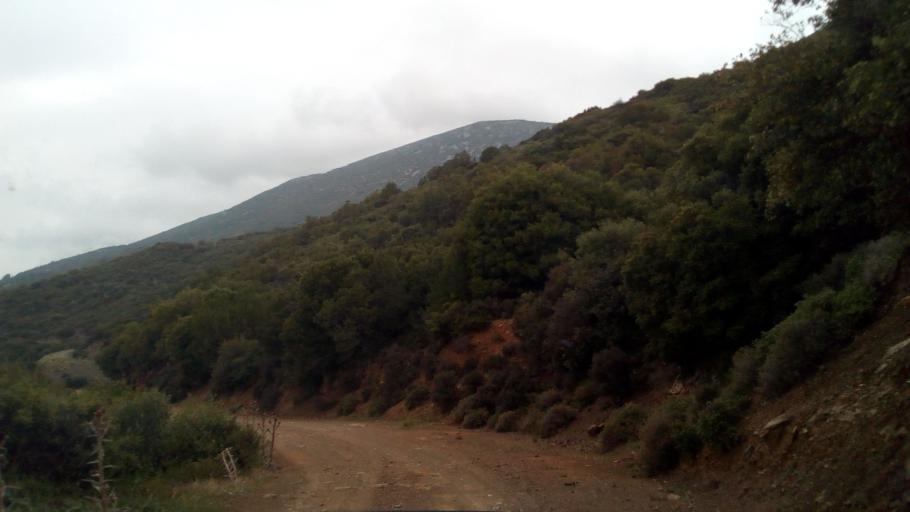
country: GR
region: West Greece
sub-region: Nomos Achaias
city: Aigio
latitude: 38.3742
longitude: 22.1563
